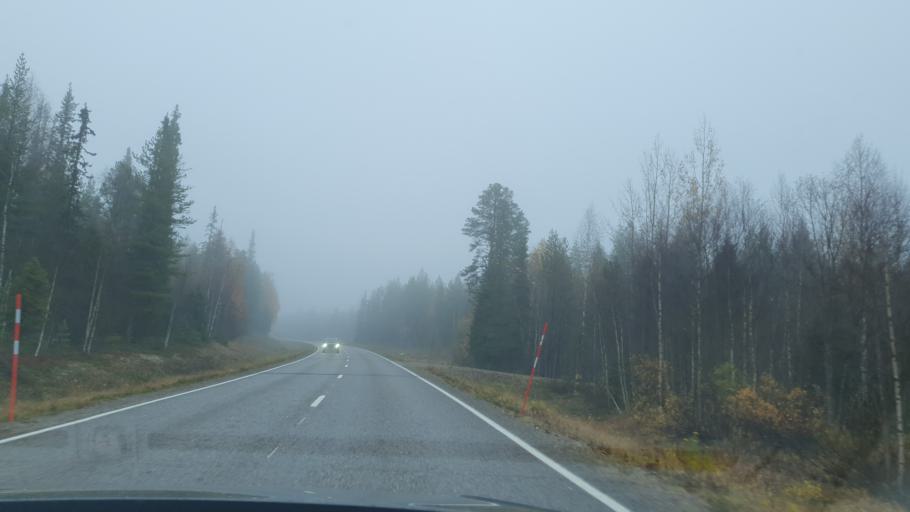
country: FI
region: Lapland
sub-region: Tunturi-Lappi
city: Kittilae
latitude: 67.6610
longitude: 24.8305
